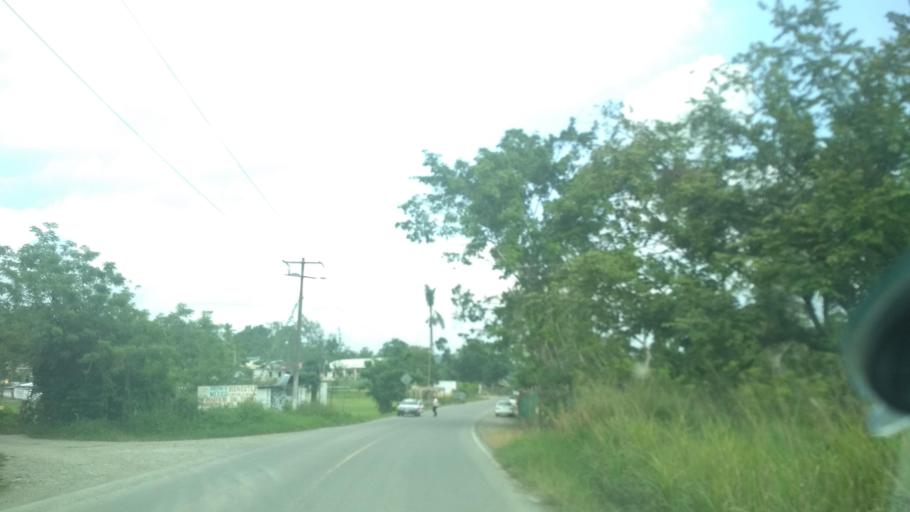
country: MX
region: Veracruz
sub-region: Poza Rica de Hidalgo
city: Arroyo del Maiz Uno
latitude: 20.5167
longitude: -97.3846
